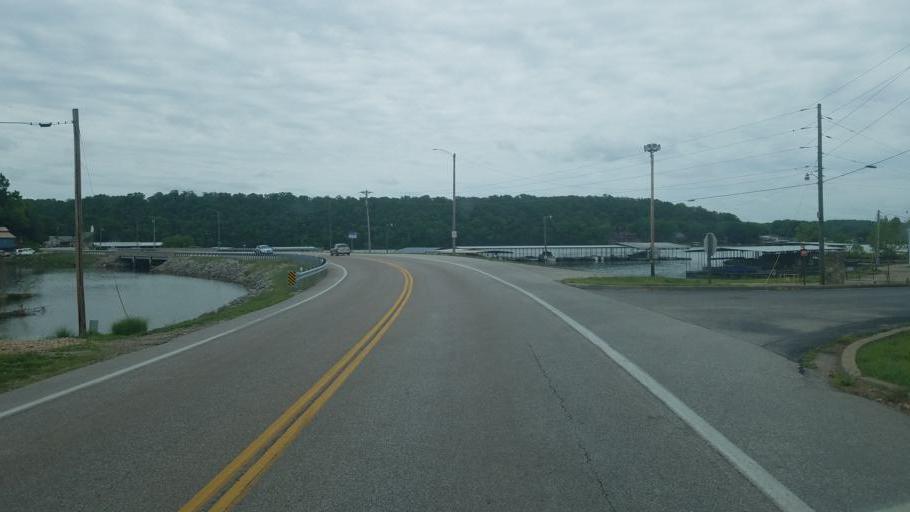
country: US
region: Missouri
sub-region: Morgan County
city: Versailles
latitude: 38.3101
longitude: -92.8236
